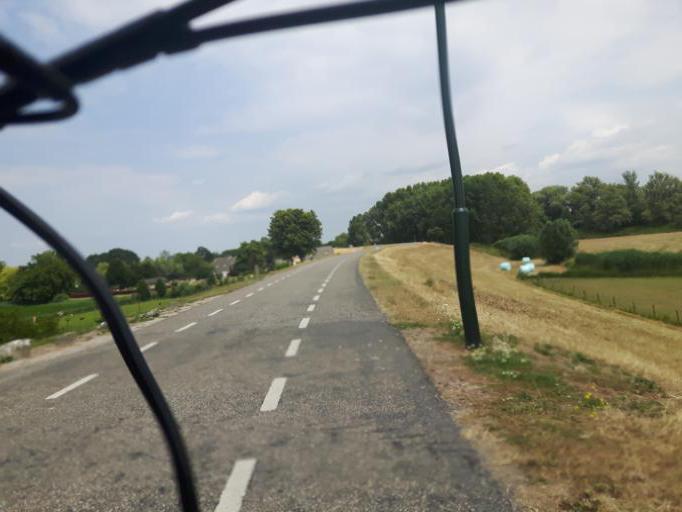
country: NL
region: Gelderland
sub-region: Gemeente Zaltbommel
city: Nederhemert
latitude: 51.8221
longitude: 5.1754
